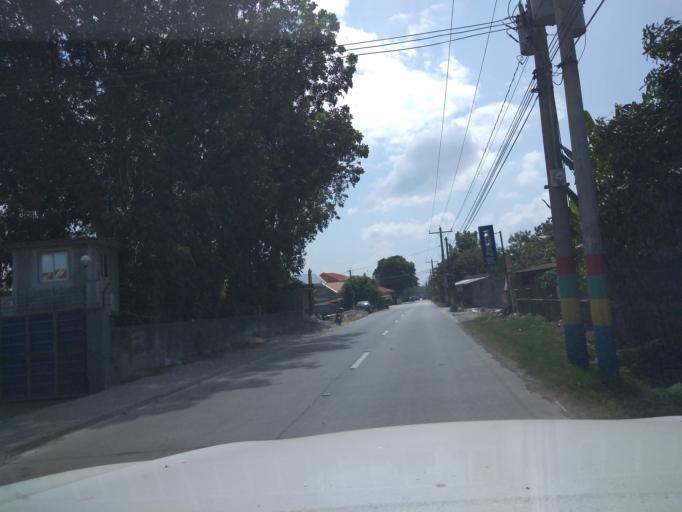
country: PH
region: Central Luzon
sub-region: Province of Pampanga
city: Lourdes
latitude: 15.0215
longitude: 120.8476
